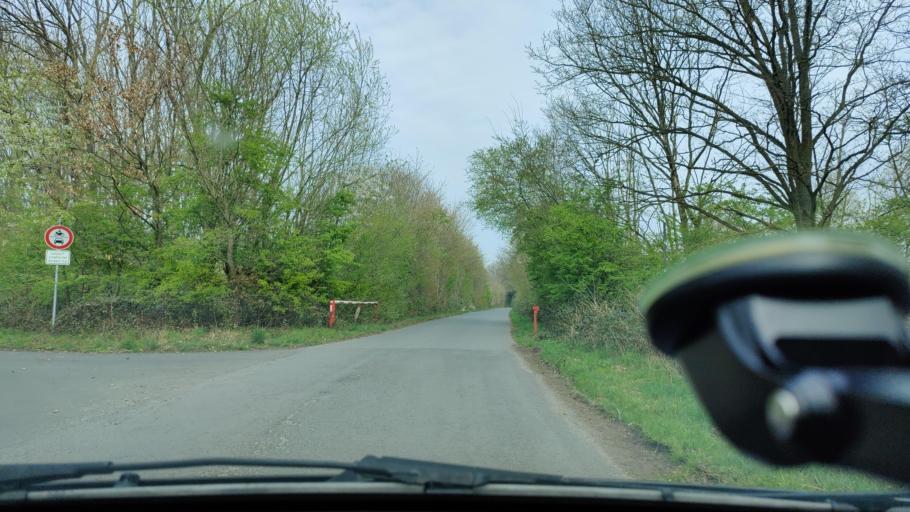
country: DE
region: North Rhine-Westphalia
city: Rheinberg
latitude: 51.5244
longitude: 6.6296
